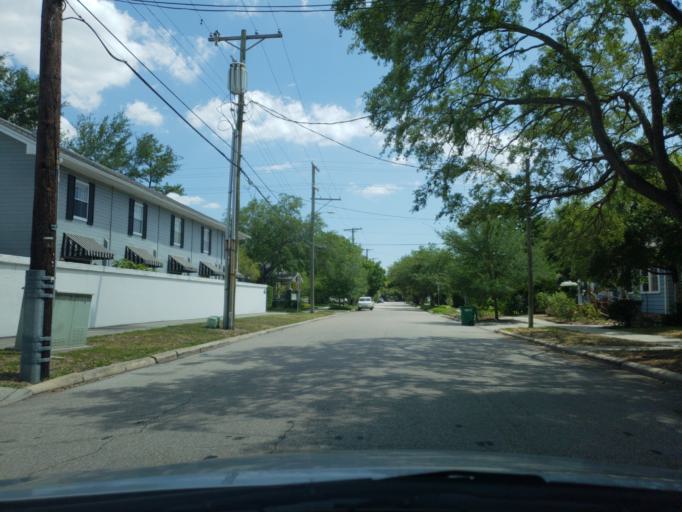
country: US
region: Florida
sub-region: Hillsborough County
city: Tampa
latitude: 27.9394
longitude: -82.4727
